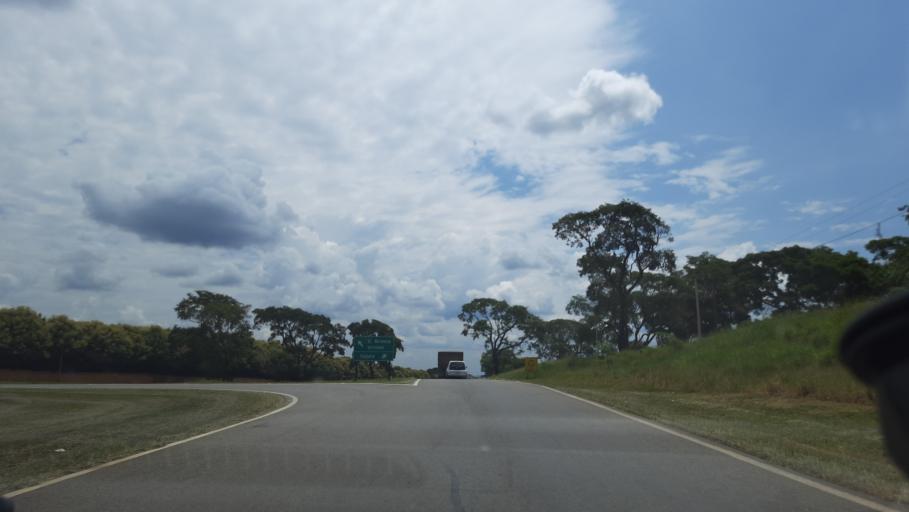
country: BR
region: Sao Paulo
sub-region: Mococa
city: Mococa
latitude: -21.5192
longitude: -47.0277
